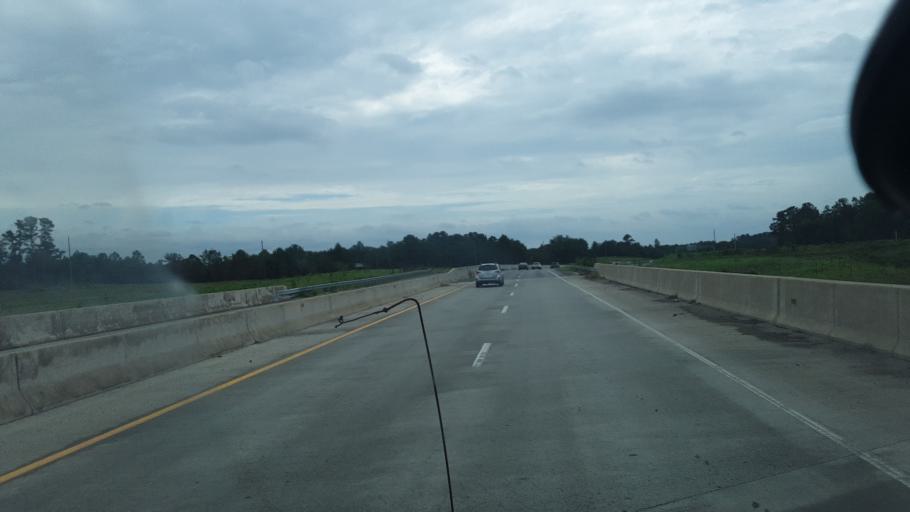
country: US
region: North Carolina
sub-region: Richmond County
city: Rockingham
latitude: 34.9941
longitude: -79.7795
